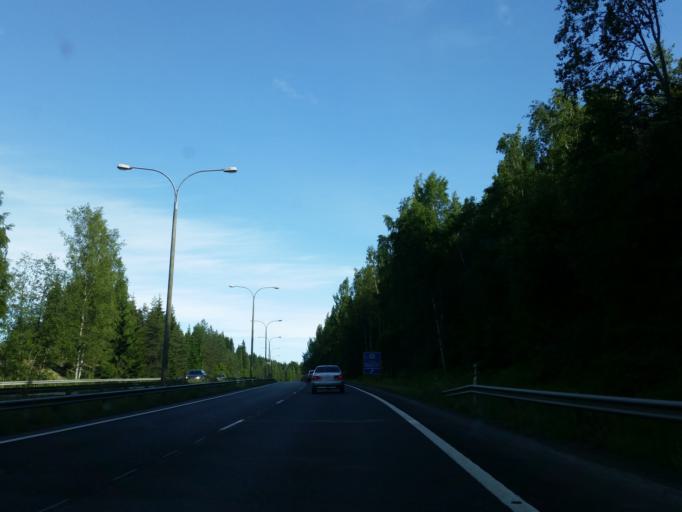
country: FI
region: Northern Savo
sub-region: Kuopio
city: Kuopio
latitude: 62.9155
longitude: 27.6803
